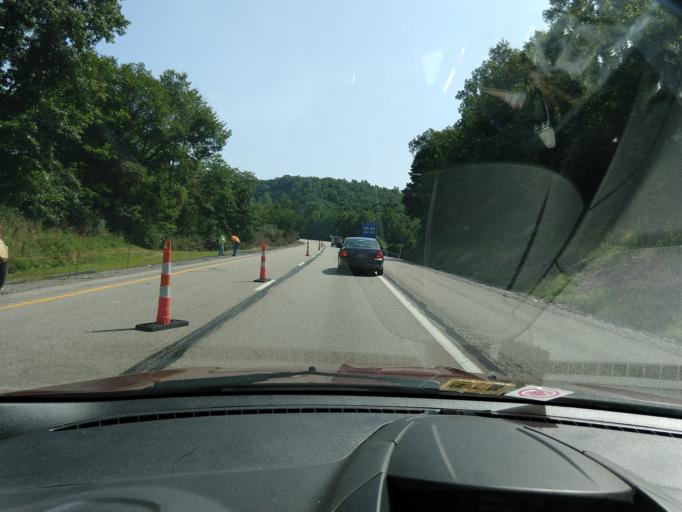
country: US
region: West Virginia
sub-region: Lewis County
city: Weston
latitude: 39.0128
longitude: -80.4525
